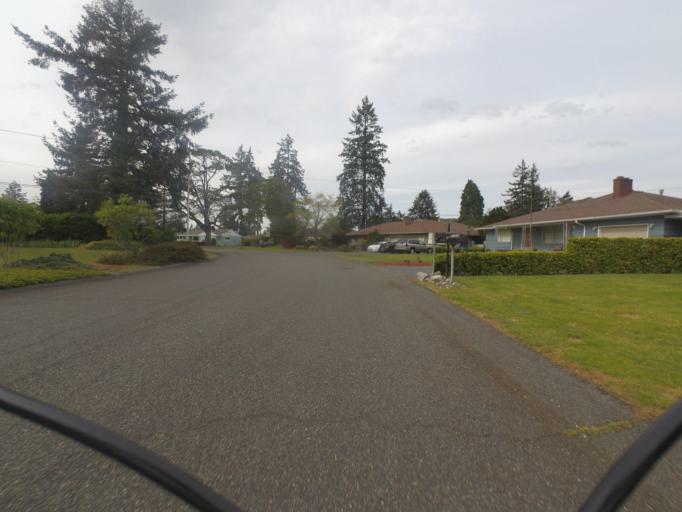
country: US
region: Washington
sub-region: Pierce County
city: McChord Air Force Base
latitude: 47.1603
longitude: -122.4915
